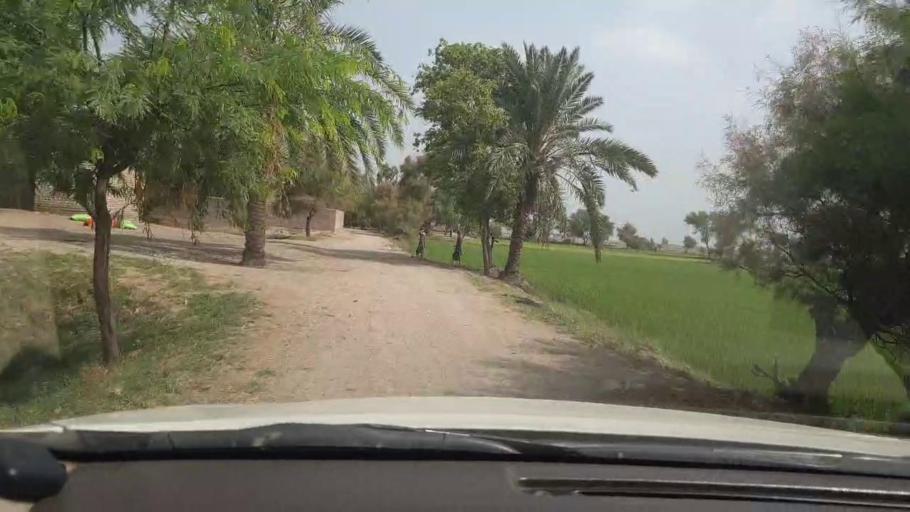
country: PK
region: Sindh
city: Shikarpur
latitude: 28.0206
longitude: 68.5910
